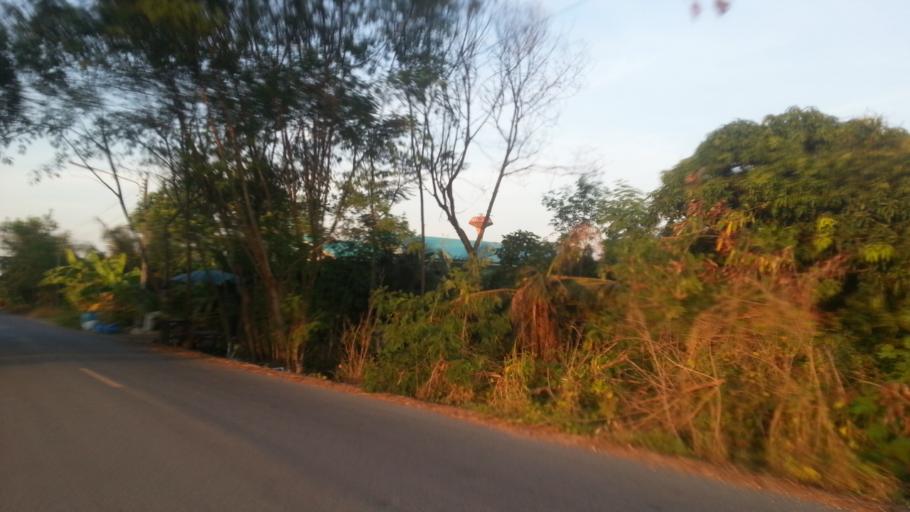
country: TH
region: Pathum Thani
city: Nong Suea
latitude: 14.0490
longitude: 100.8671
